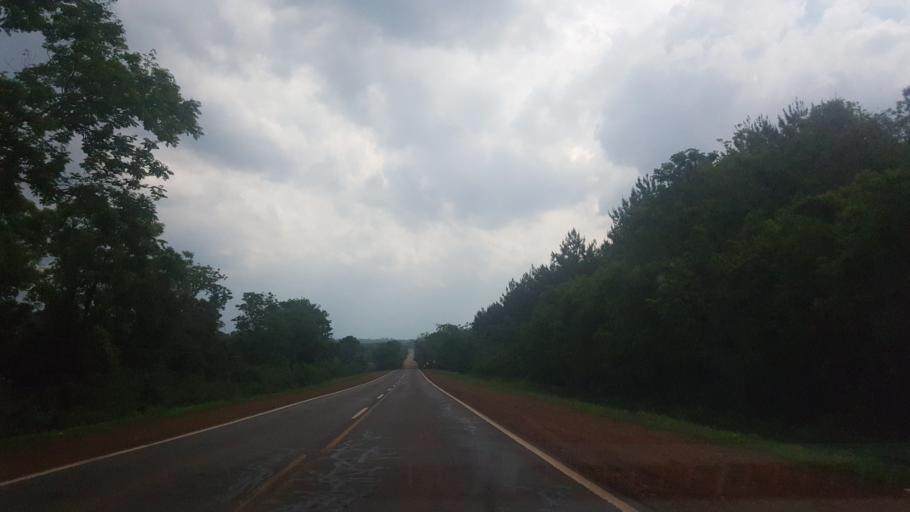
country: AR
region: Misiones
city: Santo Pipo
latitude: -27.1098
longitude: -55.3388
